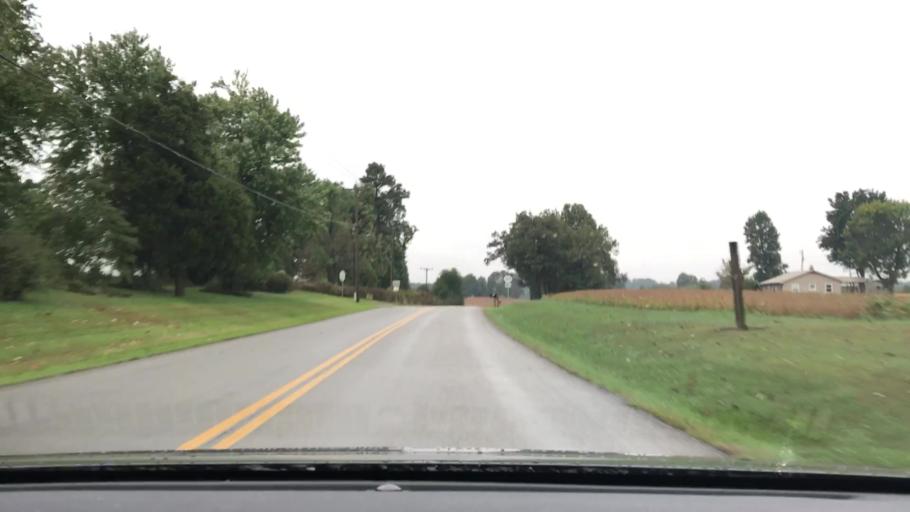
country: US
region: Kentucky
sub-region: McLean County
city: Calhoun
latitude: 37.4328
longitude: -87.2495
